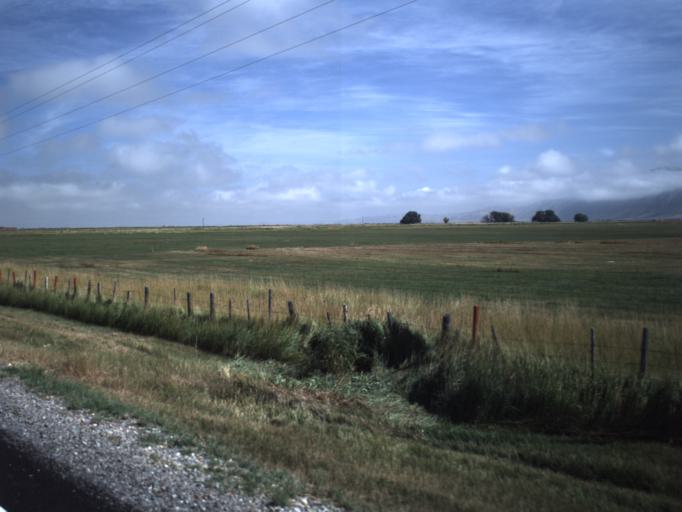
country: US
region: Utah
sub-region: Rich County
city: Randolph
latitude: 41.6325
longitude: -111.1790
